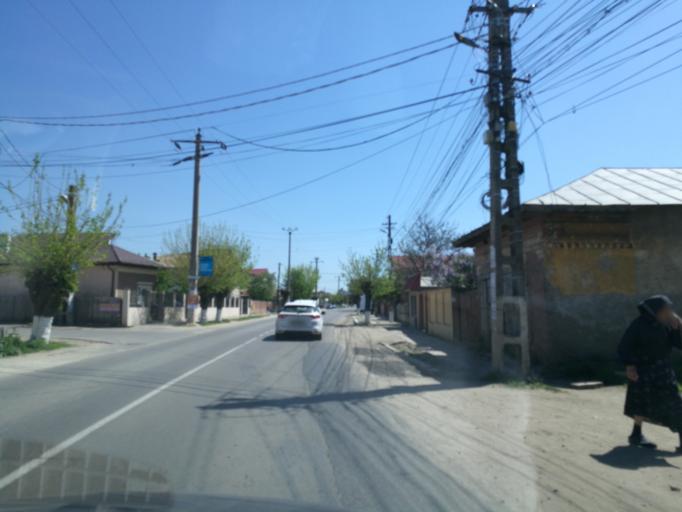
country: RO
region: Ilfov
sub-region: Comuna Berceni
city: Berceni
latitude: 44.3147
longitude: 26.1863
